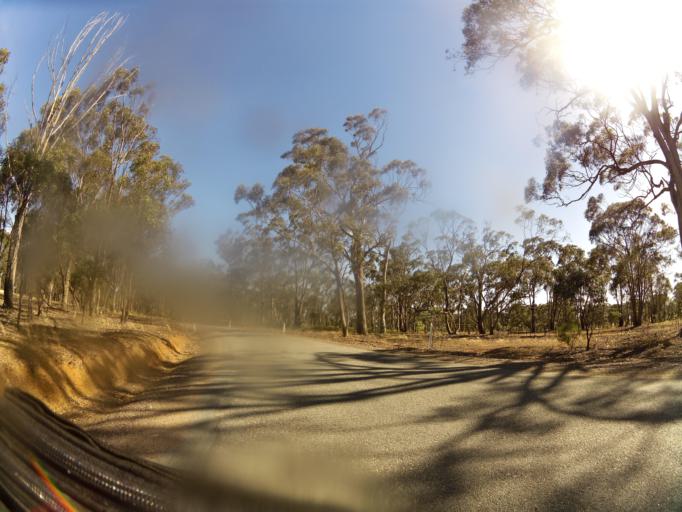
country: AU
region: Victoria
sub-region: Campaspe
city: Kyabram
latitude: -36.8768
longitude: 145.0854
